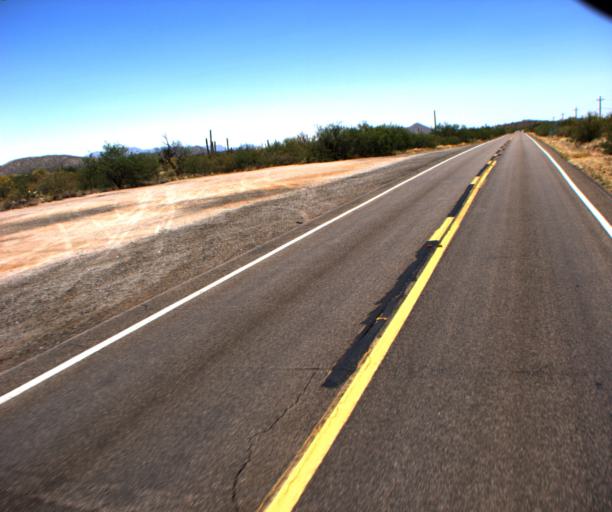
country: US
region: Arizona
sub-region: Pima County
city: Catalina
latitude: 32.6898
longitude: -111.0801
